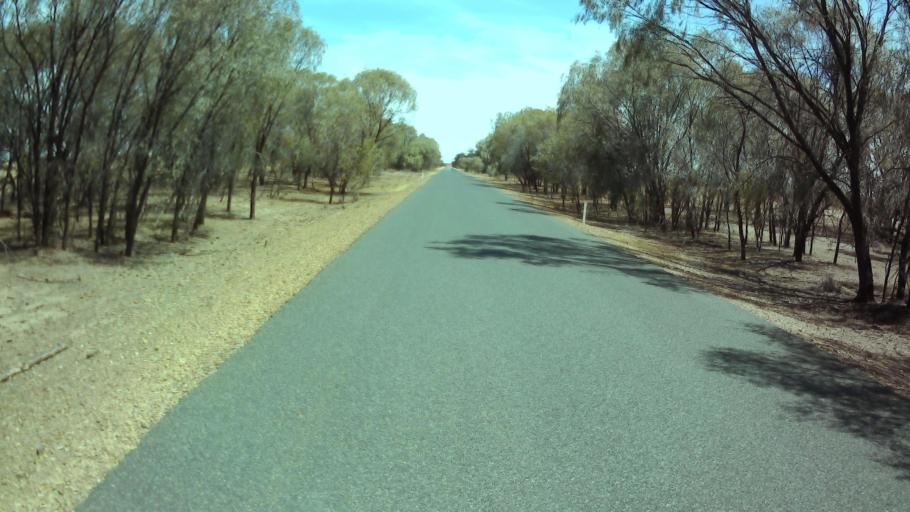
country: AU
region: New South Wales
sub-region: Weddin
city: Grenfell
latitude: -33.8750
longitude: 147.7440
